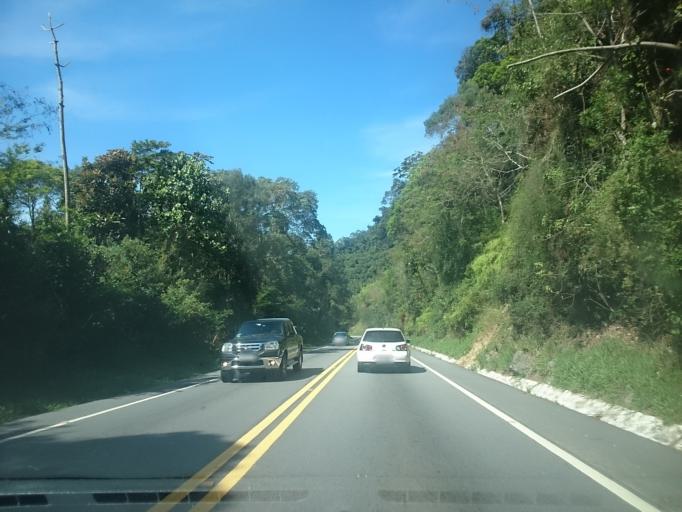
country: BR
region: Santa Catarina
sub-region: Santo Amaro Da Imperatriz
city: Santo Amaro da Imperatriz
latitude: -27.7195
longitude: -48.9205
